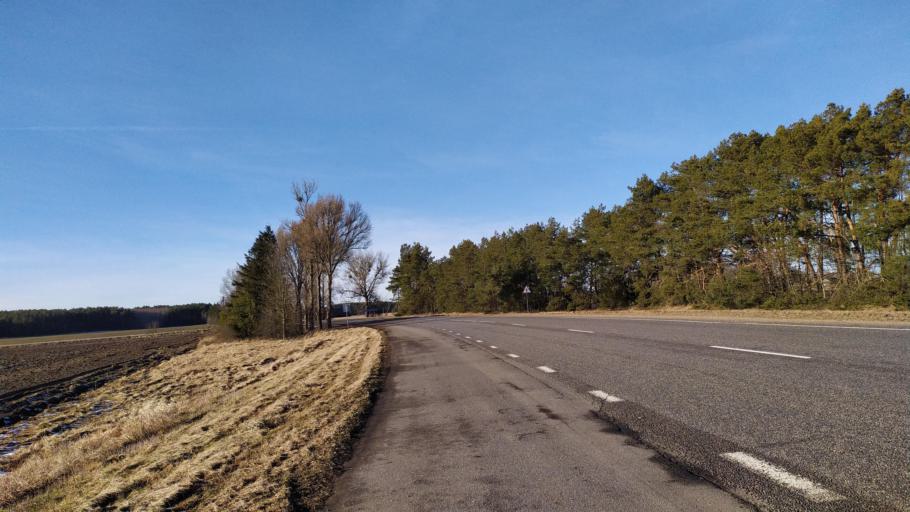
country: BY
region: Brest
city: Kamyanyets
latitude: 52.3709
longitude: 23.8834
